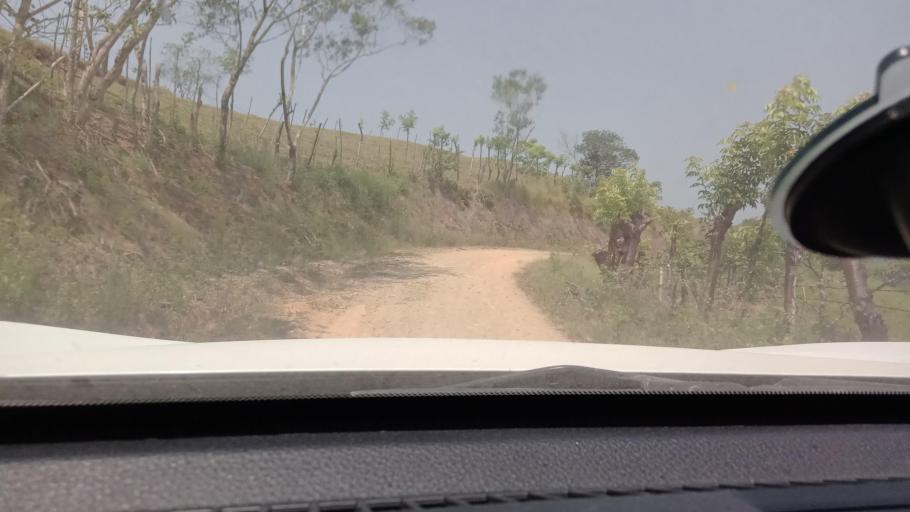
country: MX
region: Tabasco
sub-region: Huimanguillo
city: Francisco Rueda
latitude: 17.4930
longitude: -93.9207
